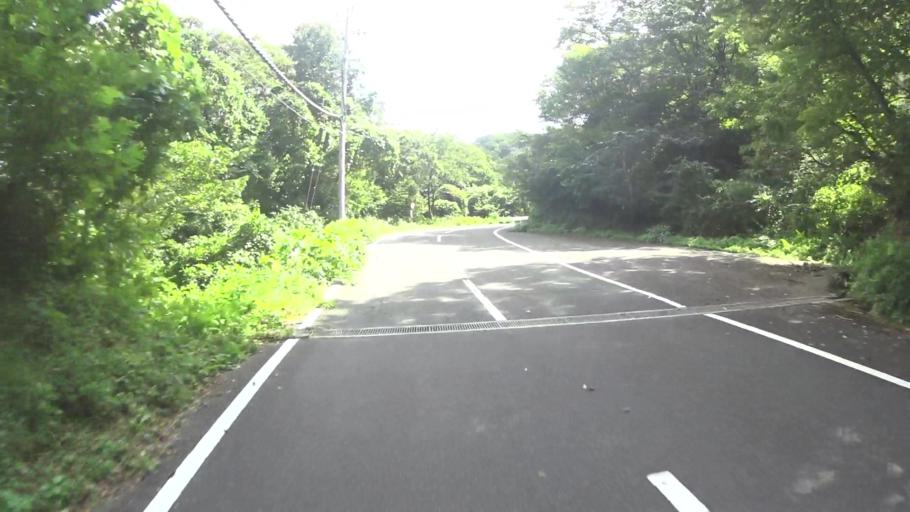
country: JP
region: Kyoto
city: Miyazu
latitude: 35.7284
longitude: 135.1852
